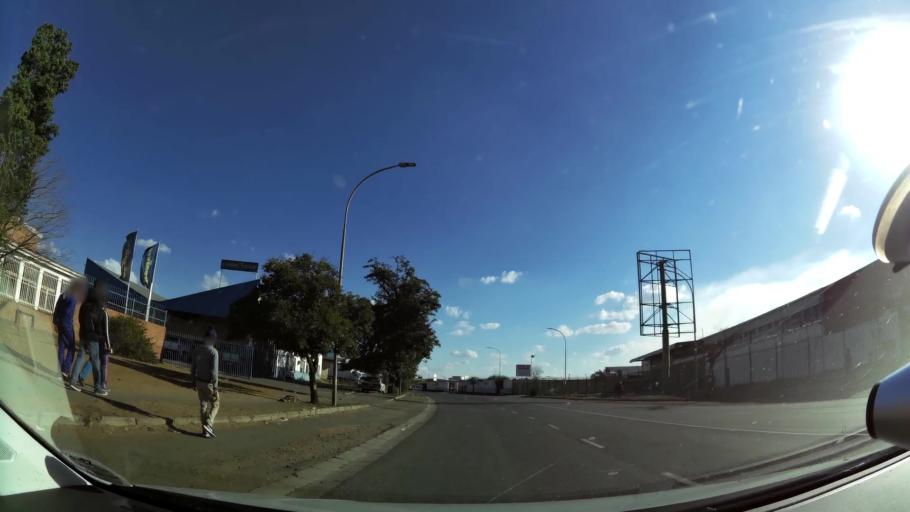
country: ZA
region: Northern Cape
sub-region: Frances Baard District Municipality
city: Kimberley
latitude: -28.7308
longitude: 24.7619
